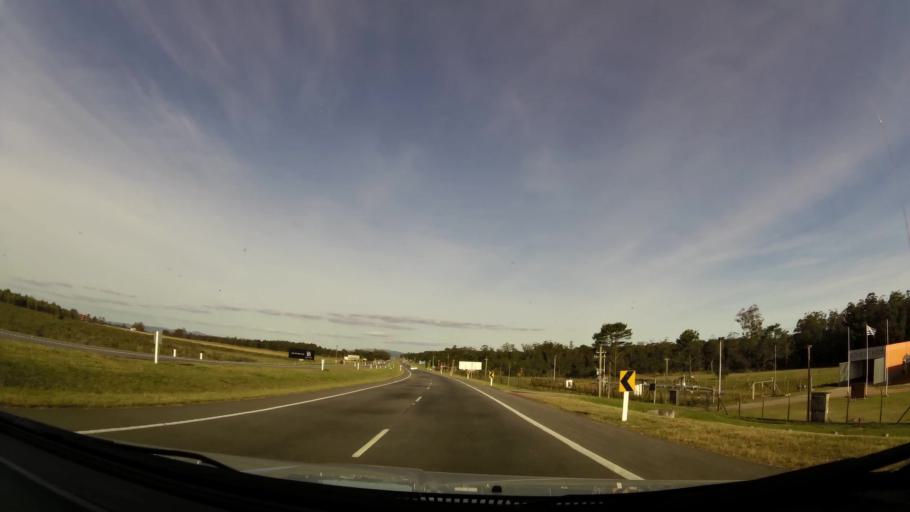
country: UY
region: Canelones
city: La Floresta
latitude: -34.7876
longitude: -55.5155
